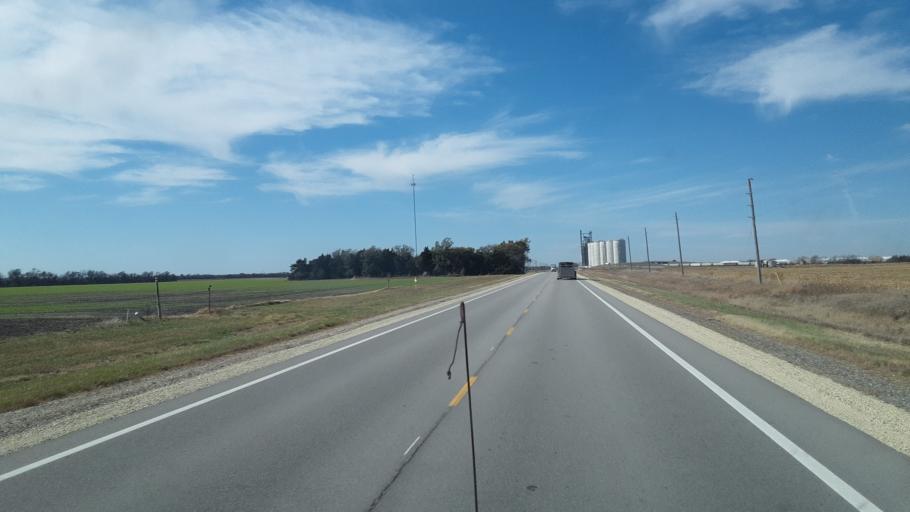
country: US
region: Kansas
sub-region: McPherson County
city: Moundridge
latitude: 38.3769
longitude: -97.4539
